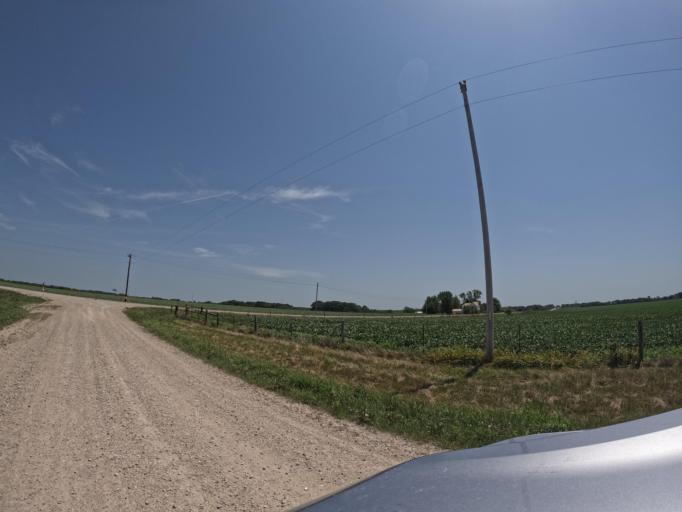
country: US
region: Iowa
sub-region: Henry County
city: Mount Pleasant
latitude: 40.9745
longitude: -91.6130
